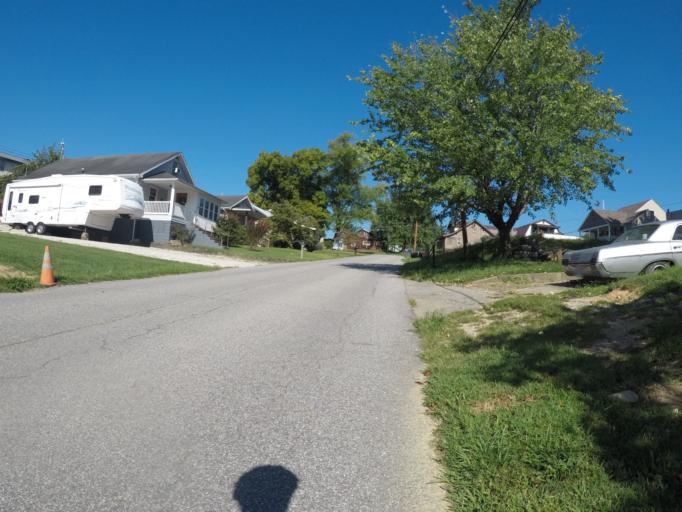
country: US
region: Kentucky
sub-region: Boyd County
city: Westwood
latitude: 38.4833
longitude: -82.6692
